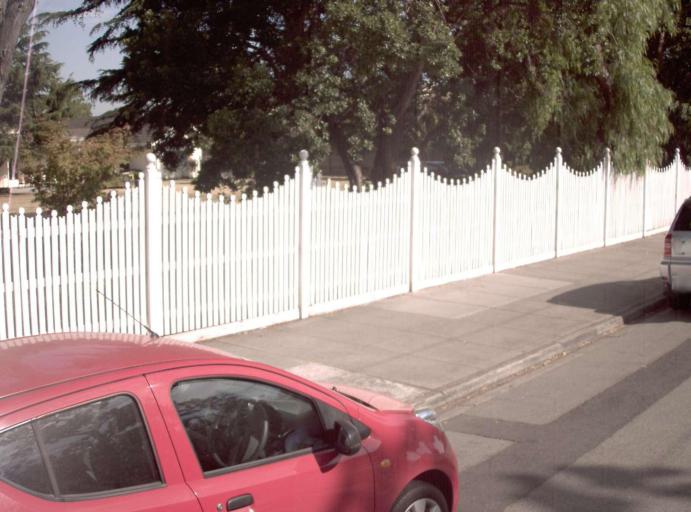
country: AU
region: Victoria
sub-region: Glen Eira
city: Caulfield North
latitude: -37.8552
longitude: 145.0295
